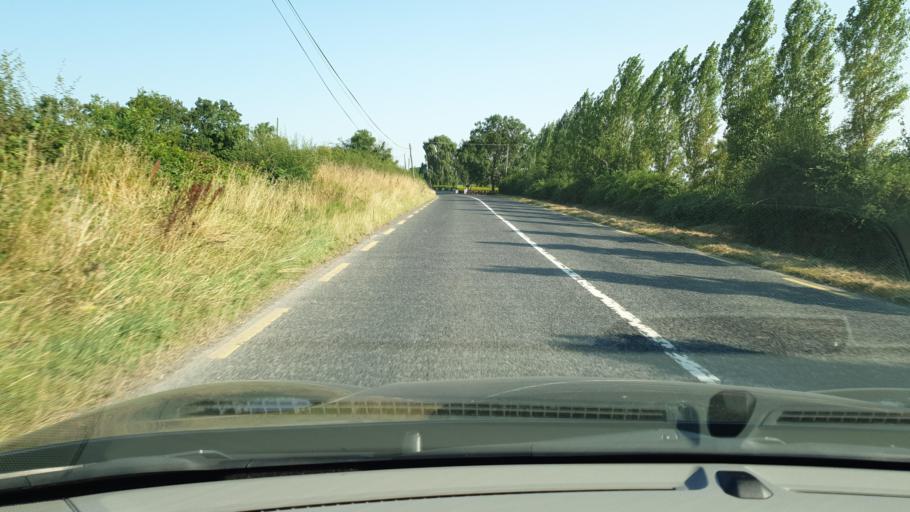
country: IE
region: Leinster
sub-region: An Mhi
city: Navan
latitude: 53.6414
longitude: -6.6187
